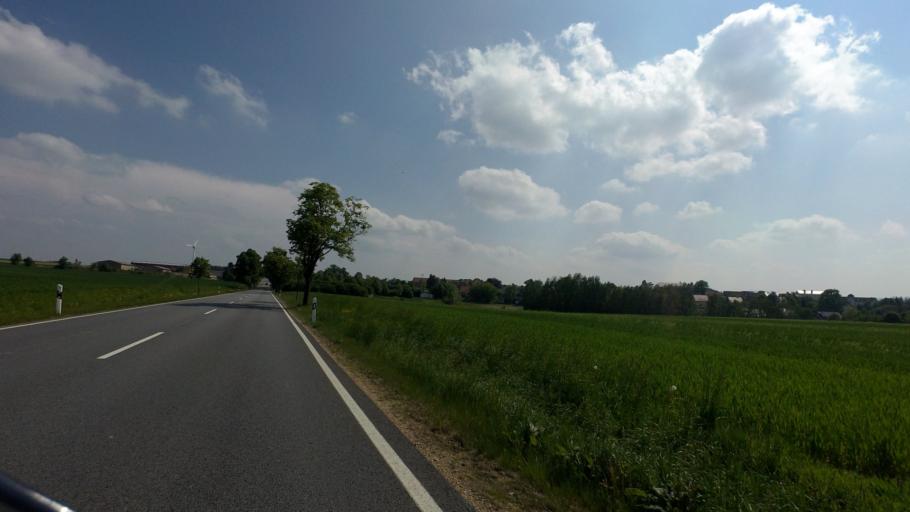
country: DE
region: Saxony
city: Weissenberg
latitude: 51.2006
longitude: 14.6666
